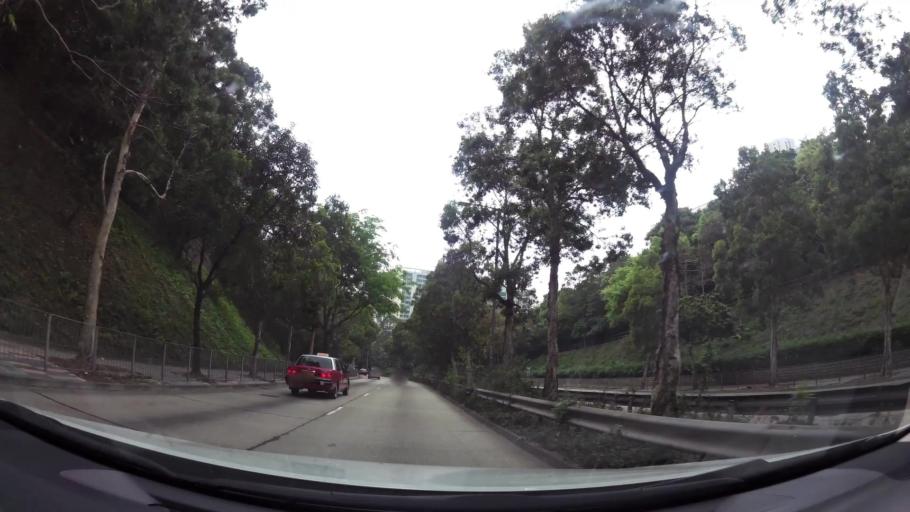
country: HK
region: Kowloon City
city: Kowloon
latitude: 22.3331
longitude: 114.2198
